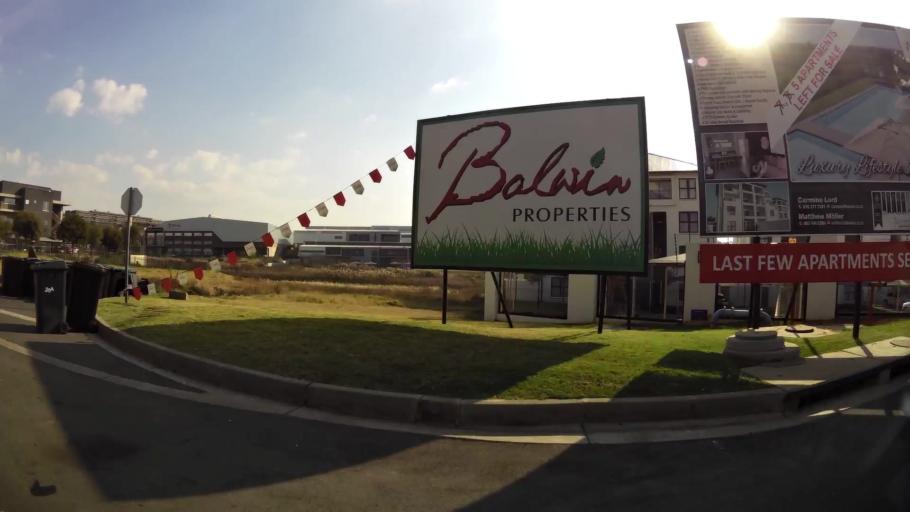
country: ZA
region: Gauteng
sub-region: City of Johannesburg Metropolitan Municipality
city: Modderfontein
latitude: -26.1030
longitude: 28.1435
